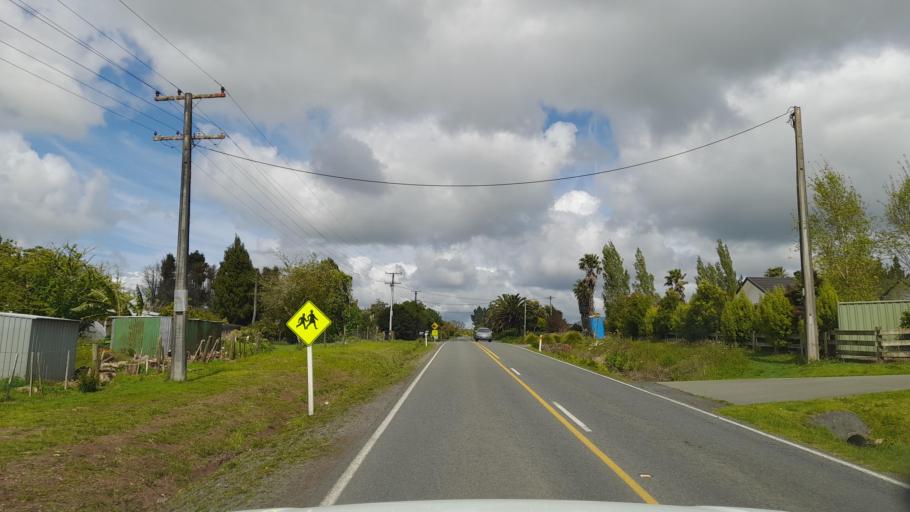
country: NZ
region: Northland
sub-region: Whangarei
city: Maungatapere
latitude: -35.6588
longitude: 174.1780
